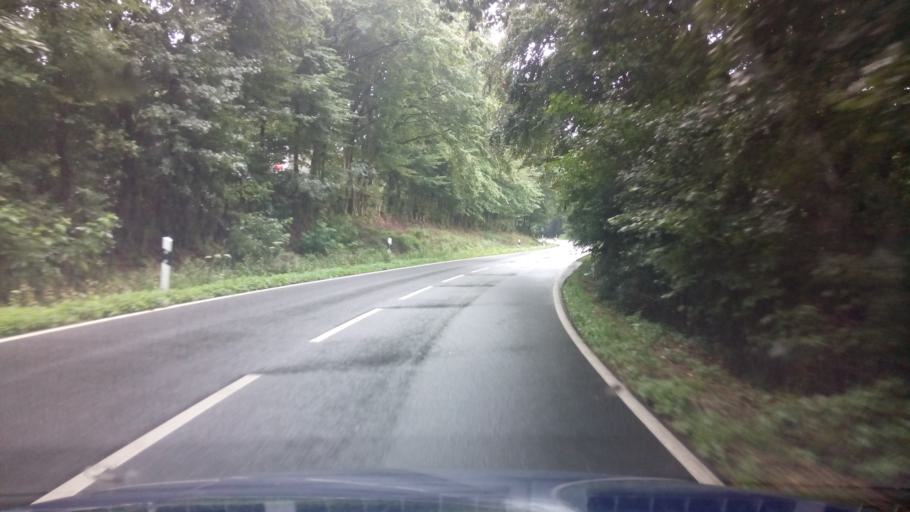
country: DE
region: Lower Saxony
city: Melle
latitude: 52.2466
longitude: 8.3077
